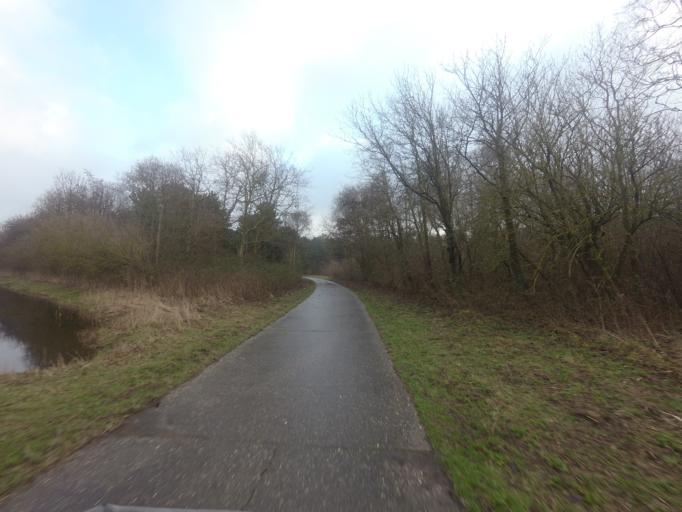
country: NL
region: North Holland
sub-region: Gemeente Texel
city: Den Burg
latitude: 53.1652
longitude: 4.8479
